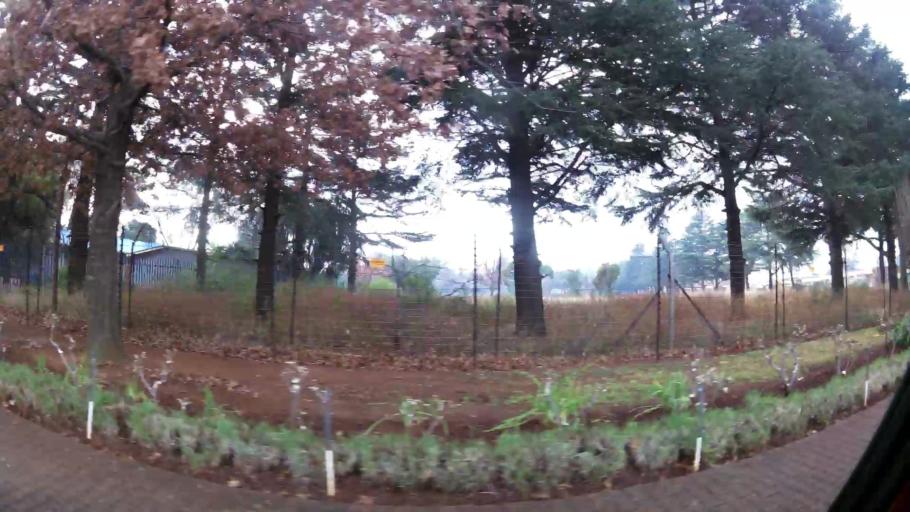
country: ZA
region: Gauteng
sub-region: Sedibeng District Municipality
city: Vanderbijlpark
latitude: -26.7044
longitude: 27.8312
